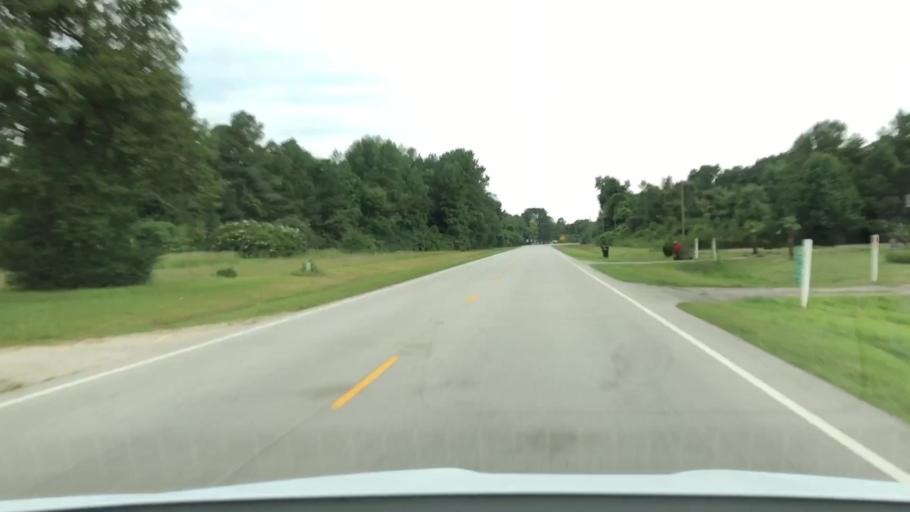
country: US
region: North Carolina
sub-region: Jones County
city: Trenton
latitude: 35.0164
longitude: -77.2979
